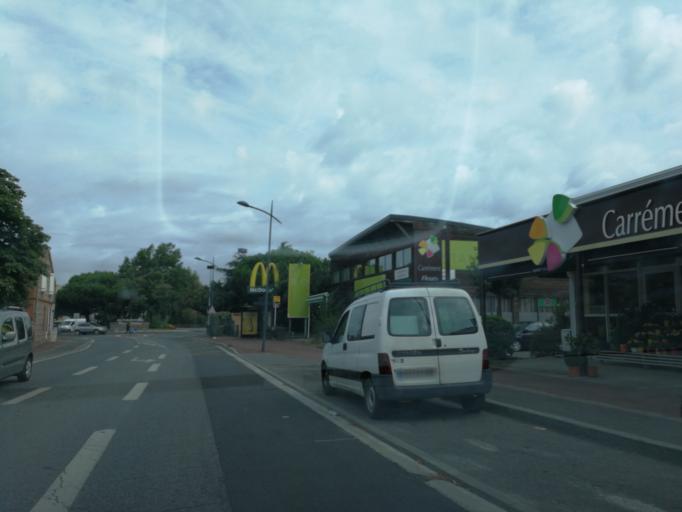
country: FR
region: Midi-Pyrenees
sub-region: Departement de la Haute-Garonne
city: Aucamville
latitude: 43.6609
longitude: 1.4316
